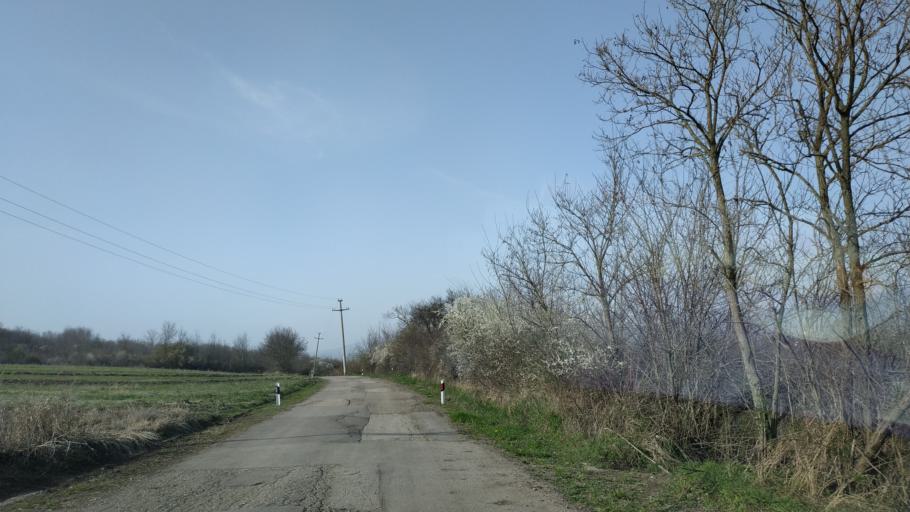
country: RS
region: Central Serbia
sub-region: Nisavski Okrug
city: Aleksinac
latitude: 43.5146
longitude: 21.6480
